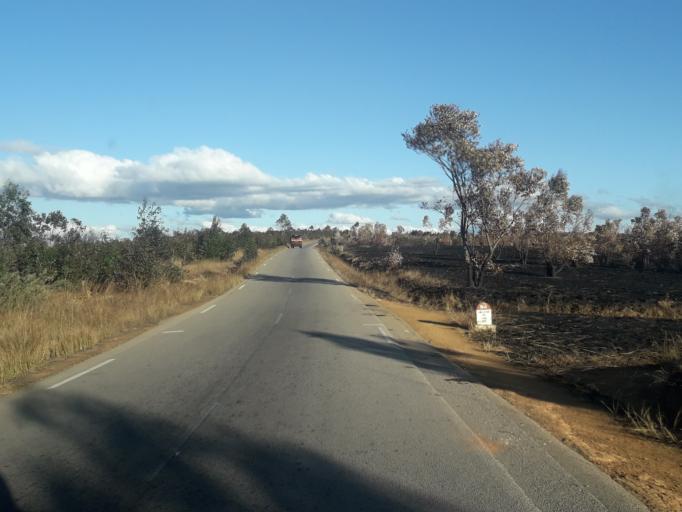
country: MG
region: Analamanga
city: Ankazobe
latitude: -18.1275
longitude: 47.2173
